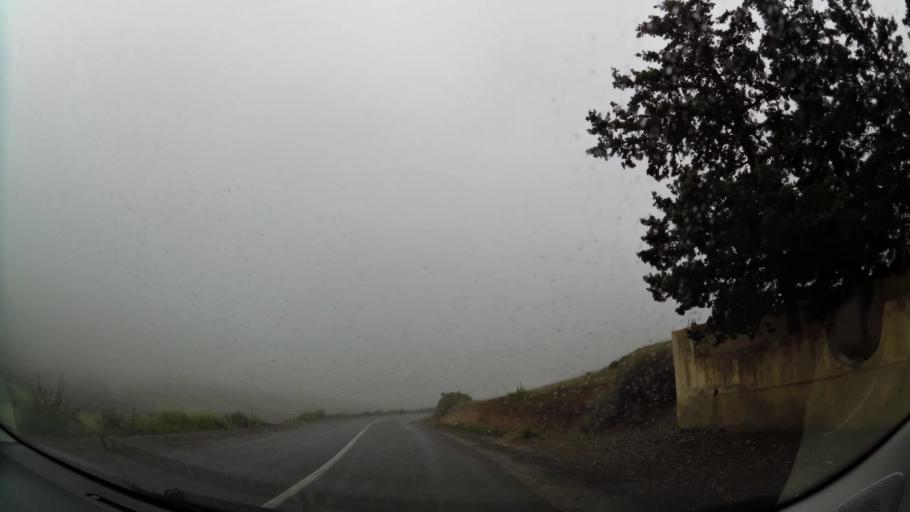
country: MA
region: Oriental
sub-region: Nador
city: Boudinar
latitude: 35.1374
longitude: -3.6006
